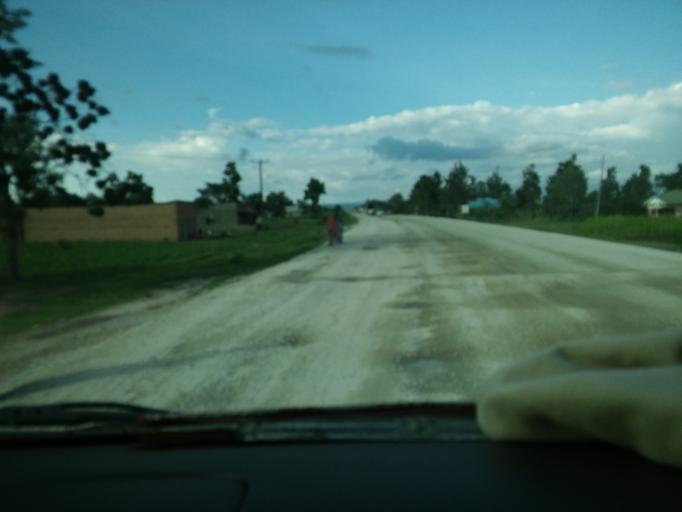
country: UG
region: Eastern Region
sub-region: Mbale District
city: Mbale
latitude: 1.0573
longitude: 34.0710
